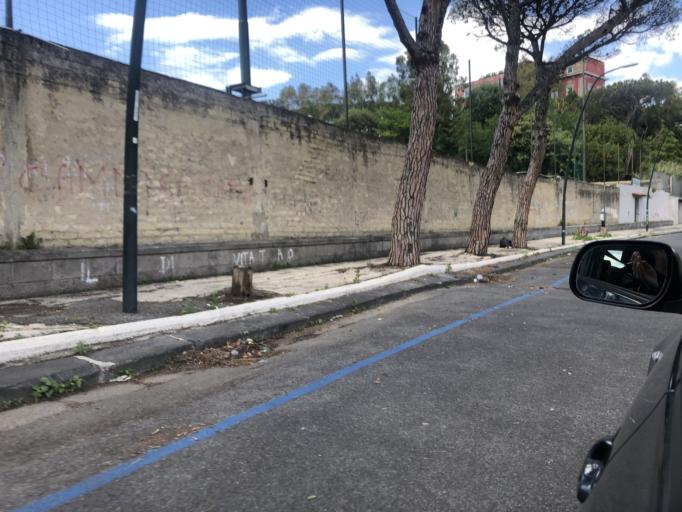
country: IT
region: Campania
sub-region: Provincia di Napoli
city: Bagnoli
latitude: 40.8002
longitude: 14.1875
